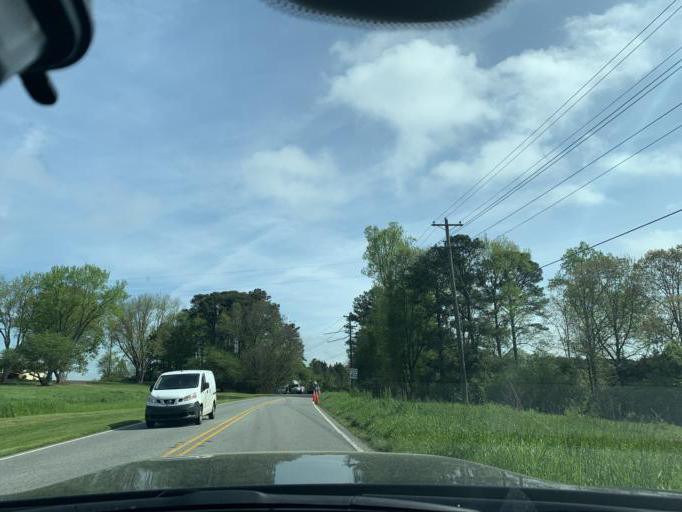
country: US
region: Georgia
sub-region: Forsyth County
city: Cumming
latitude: 34.2459
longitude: -84.0828
